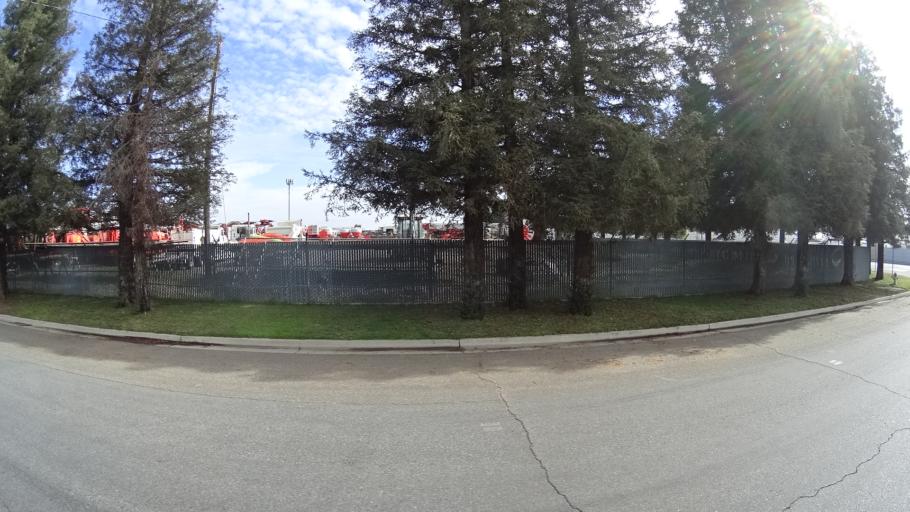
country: US
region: California
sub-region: Kern County
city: Greenacres
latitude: 35.3945
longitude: -119.0833
